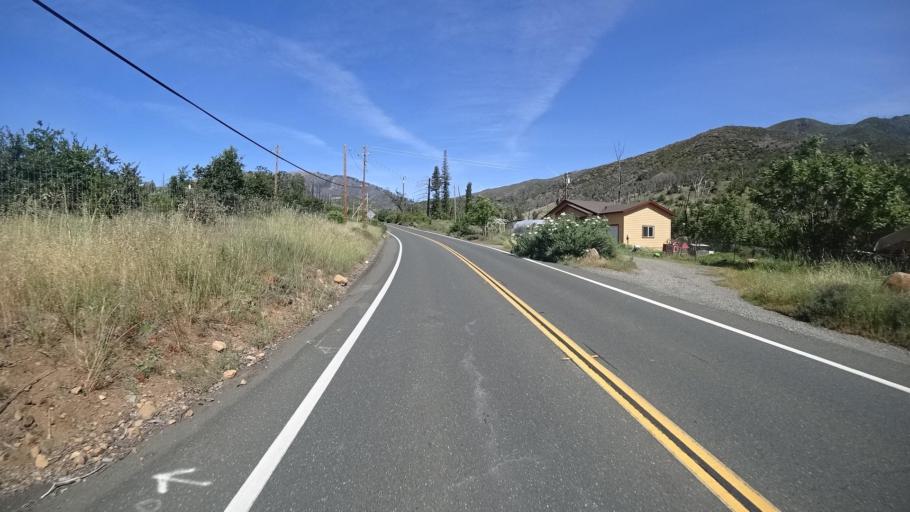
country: US
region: California
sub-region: Lake County
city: Cobb
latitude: 38.7793
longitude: -122.6825
